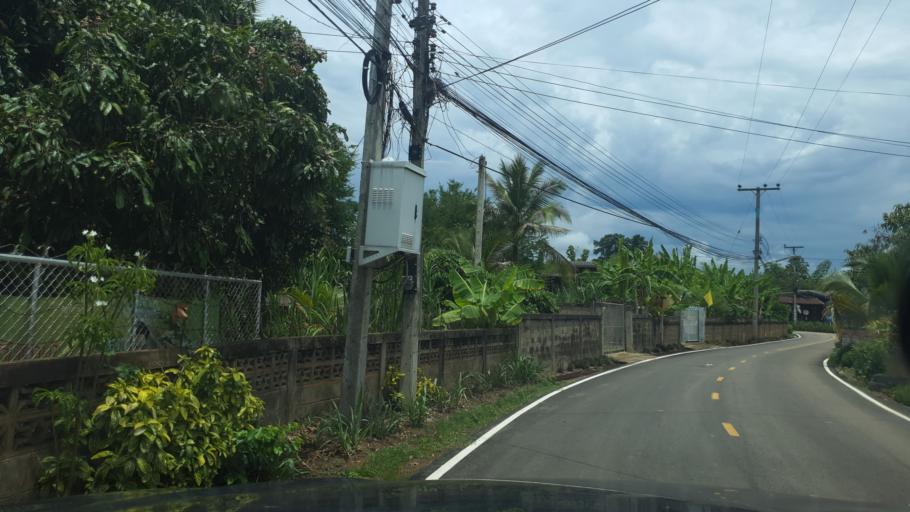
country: TH
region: Lampang
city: Ko Kha
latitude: 18.1993
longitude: 99.3305
